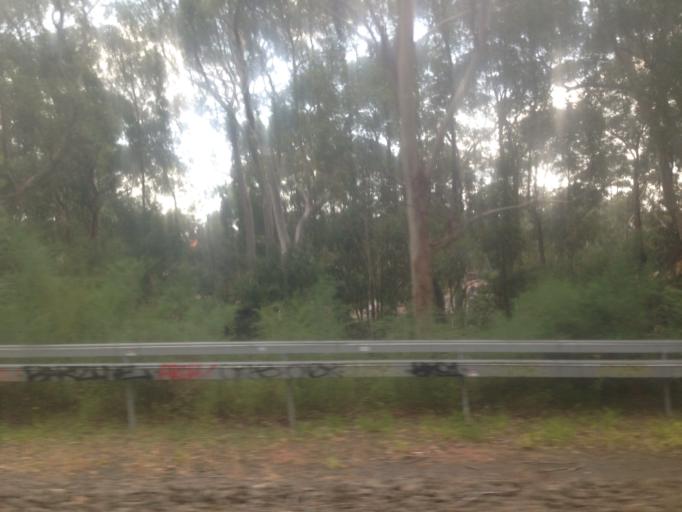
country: AU
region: New South Wales
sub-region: Willoughby
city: Artarmon
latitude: -33.8096
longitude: 151.1865
